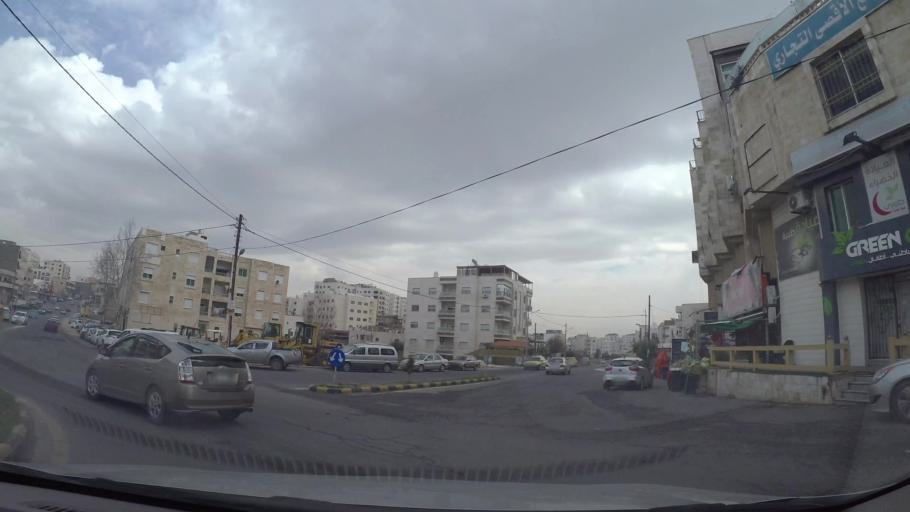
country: JO
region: Amman
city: Umm as Summaq
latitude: 31.9072
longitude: 35.8476
